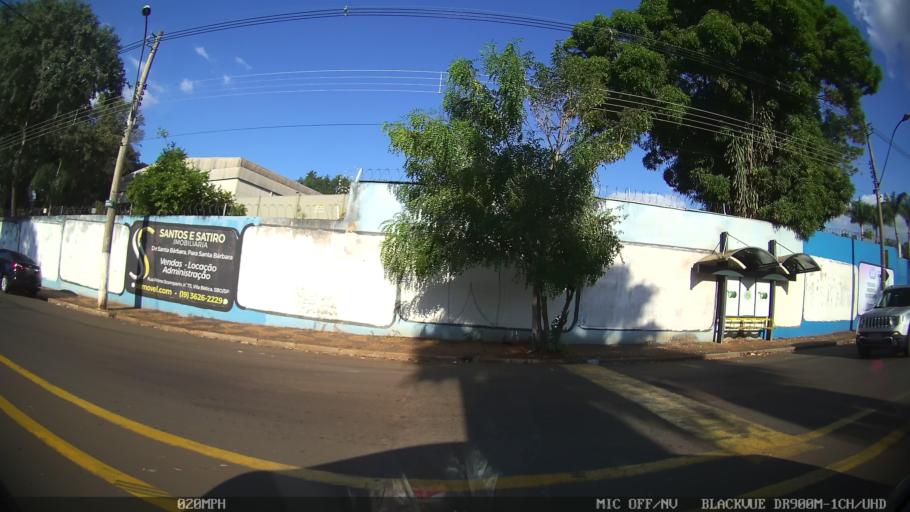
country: BR
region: Sao Paulo
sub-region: Santa Barbara D'Oeste
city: Santa Barbara d'Oeste
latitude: -22.7524
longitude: -47.4261
